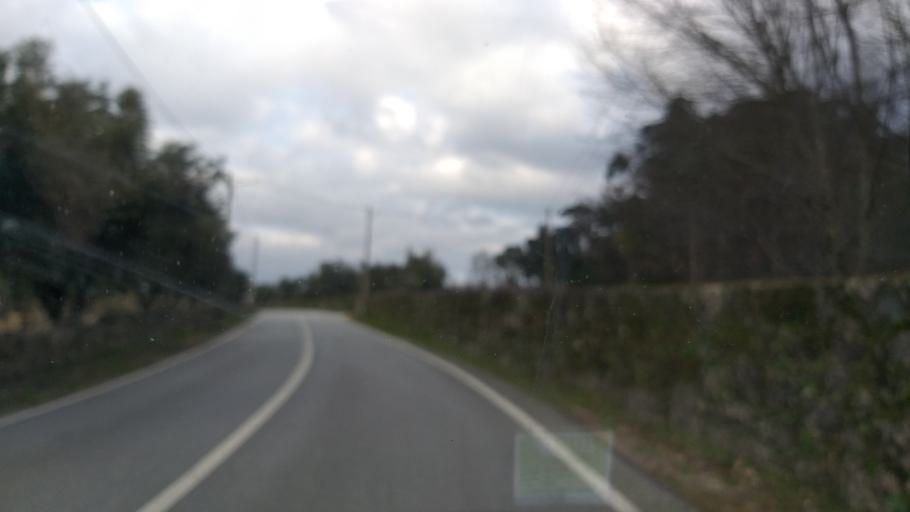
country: PT
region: Guarda
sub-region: Manteigas
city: Manteigas
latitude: 40.5064
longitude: -7.6095
